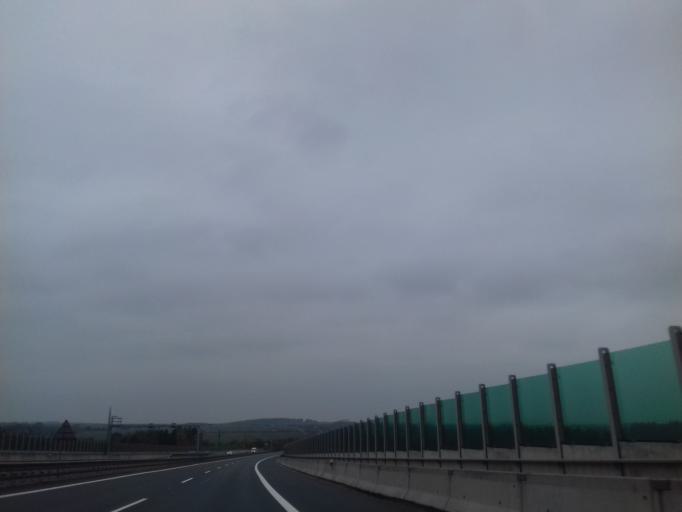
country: CZ
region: Plzensky
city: Stenovice
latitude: 49.6812
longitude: 13.3997
